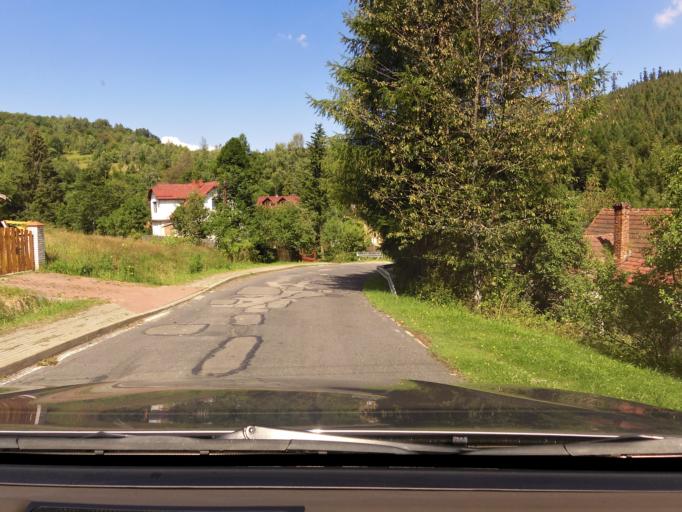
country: PL
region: Silesian Voivodeship
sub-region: Powiat cieszynski
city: Koniakow
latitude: 49.5120
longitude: 18.9650
